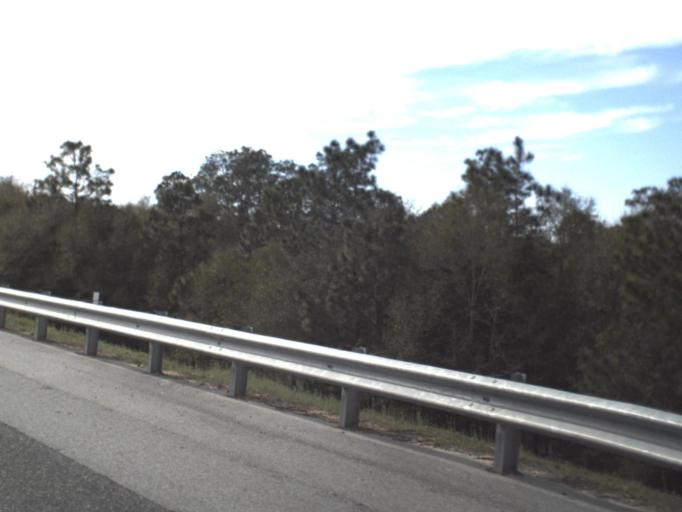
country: US
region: Florida
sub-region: Bay County
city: Youngstown
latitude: 30.5272
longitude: -85.4030
